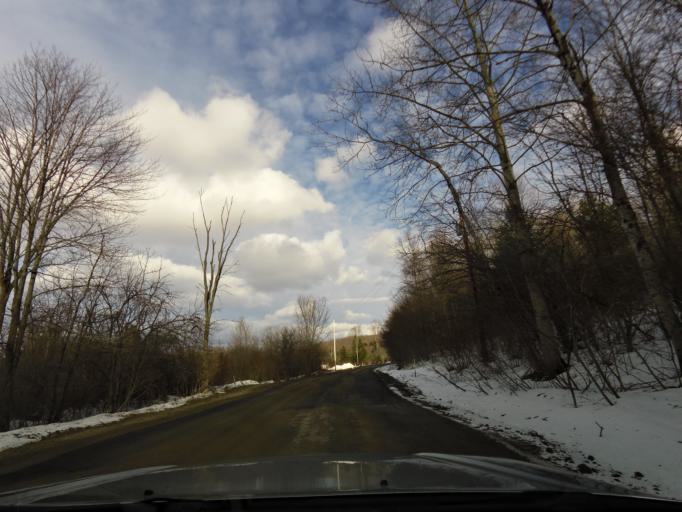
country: US
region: New York
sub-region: Cattaraugus County
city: Franklinville
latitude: 42.3401
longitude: -78.4349
